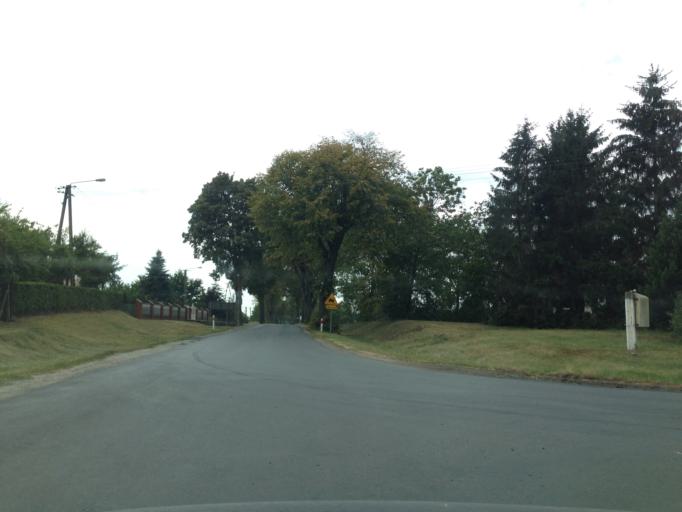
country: PL
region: Kujawsko-Pomorskie
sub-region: Powiat golubsko-dobrzynski
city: Kowalewo Pomorskie
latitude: 53.2013
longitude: 18.8153
